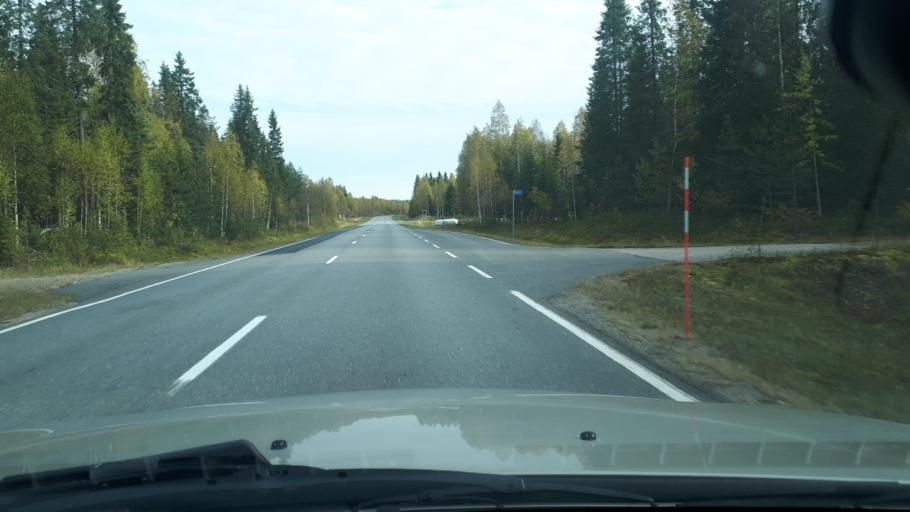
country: FI
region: Lapland
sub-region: Rovaniemi
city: Ranua
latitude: 65.9759
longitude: 26.1173
